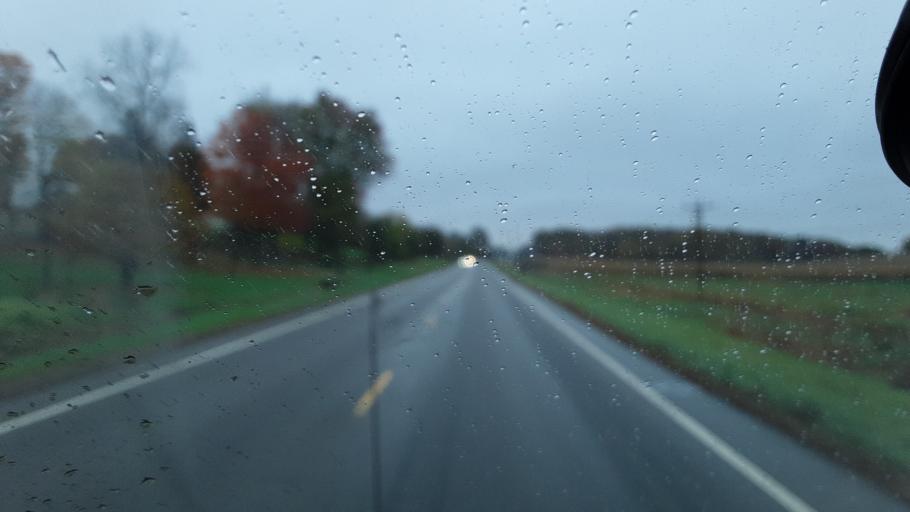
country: US
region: Ohio
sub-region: Morrow County
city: Mount Gilead
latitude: 40.5117
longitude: -82.7367
